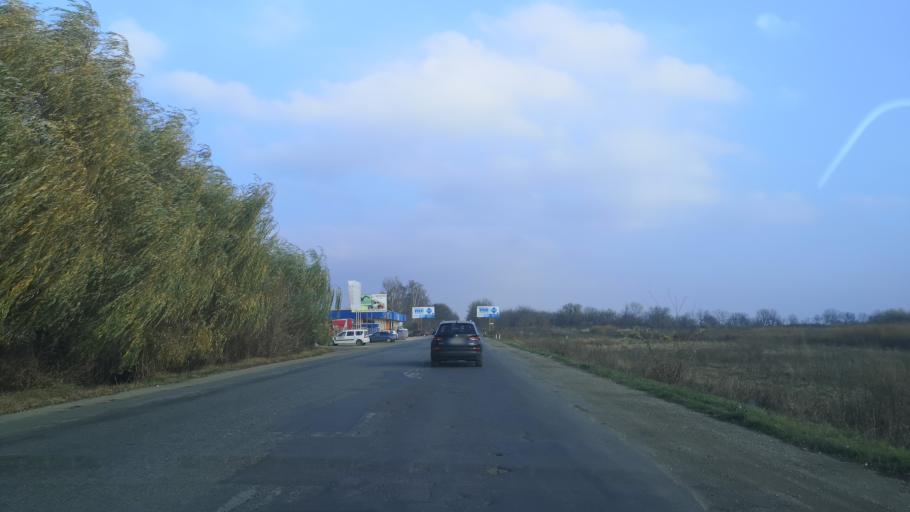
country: MD
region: Balti
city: Balti
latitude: 47.7803
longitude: 27.9572
